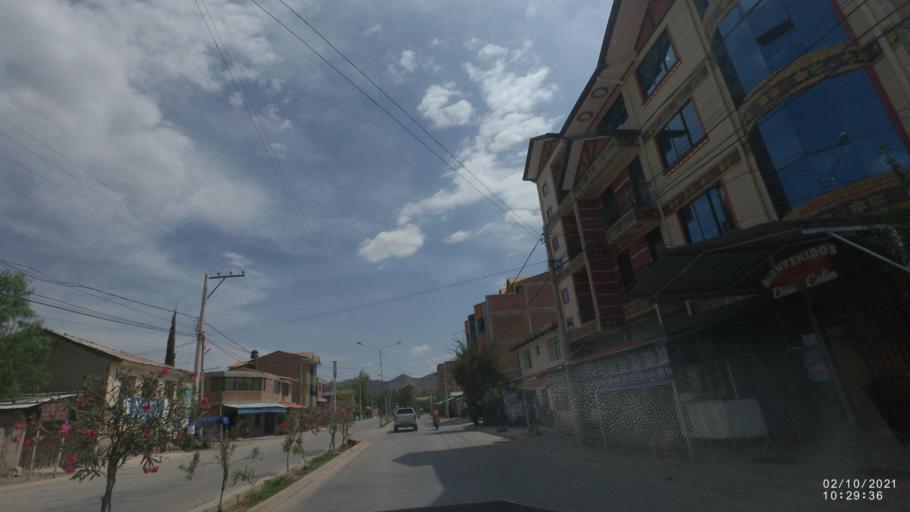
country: BO
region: Cochabamba
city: Capinota
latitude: -17.7041
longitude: -66.2659
